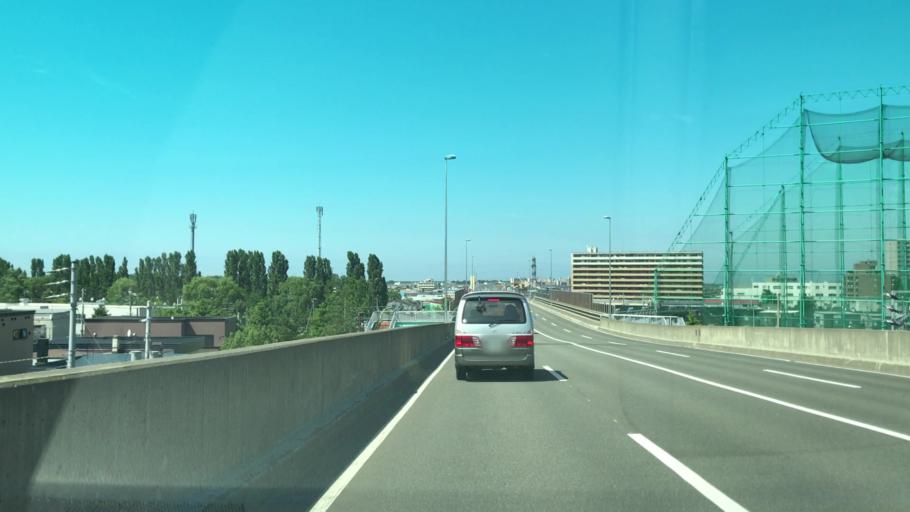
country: JP
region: Hokkaido
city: Sapporo
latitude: 43.1228
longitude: 141.2359
